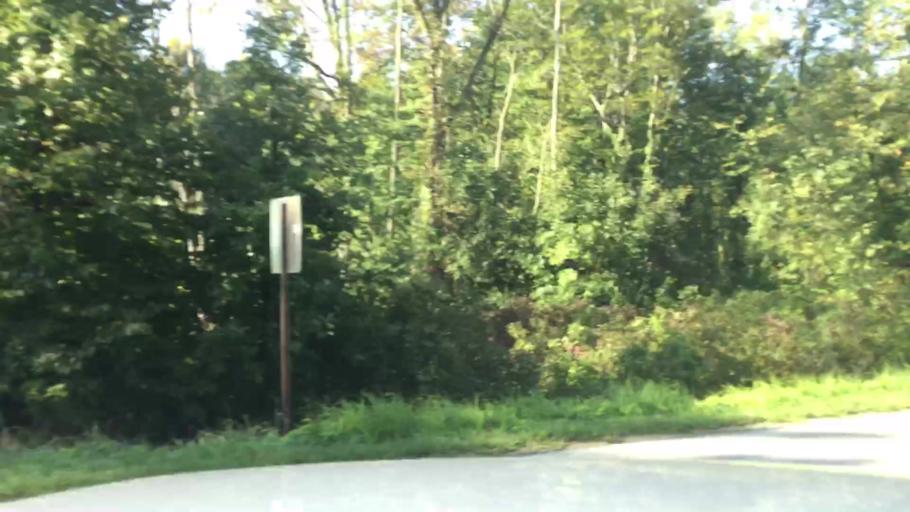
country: US
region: Michigan
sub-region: Lenawee County
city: Manitou Beach-Devils Lake
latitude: 41.9426
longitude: -84.3415
